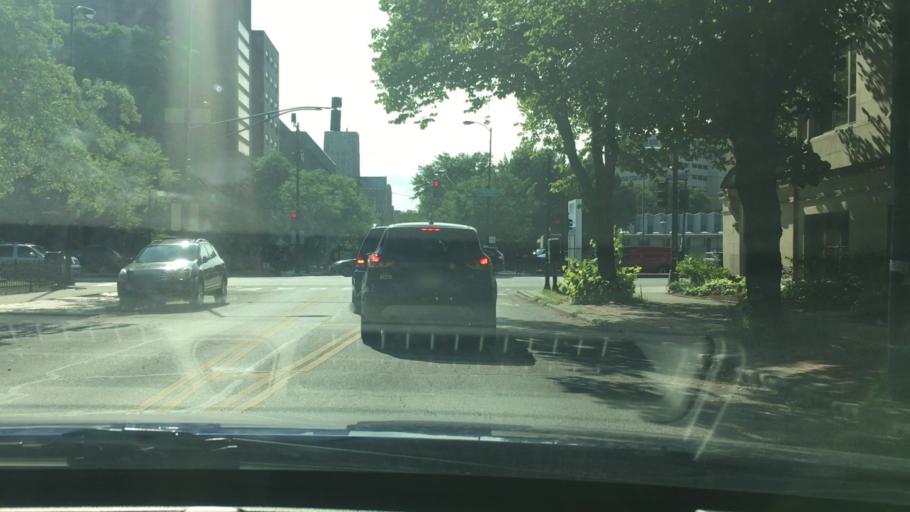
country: US
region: Illinois
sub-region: Cook County
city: Chicago
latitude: 41.8716
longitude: -87.6659
